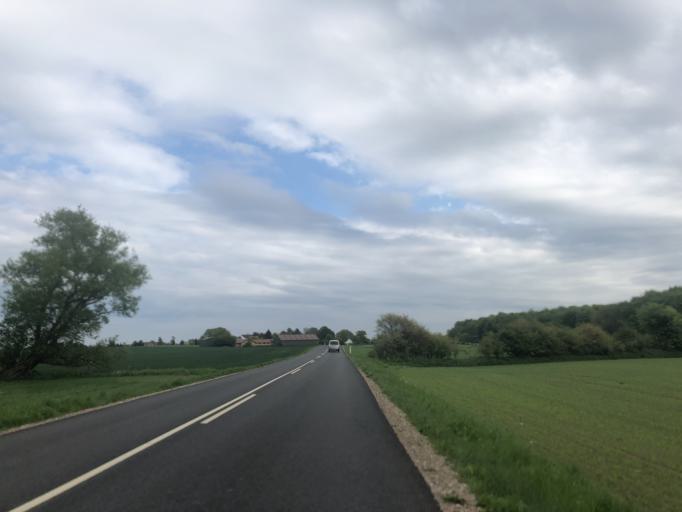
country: DK
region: Zealand
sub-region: Koge Kommune
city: Koge
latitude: 55.4718
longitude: 12.1469
